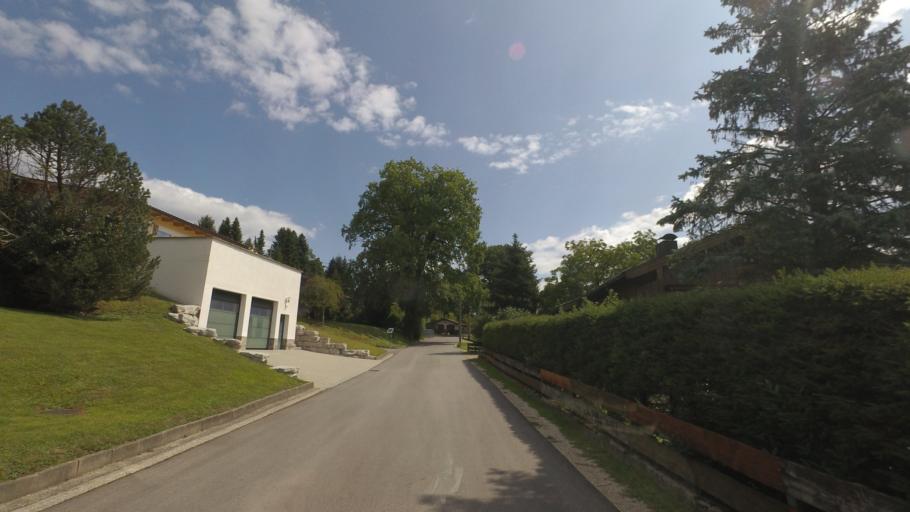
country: DE
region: Bavaria
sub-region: Upper Bavaria
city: Vachendorf
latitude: 47.8512
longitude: 12.5804
